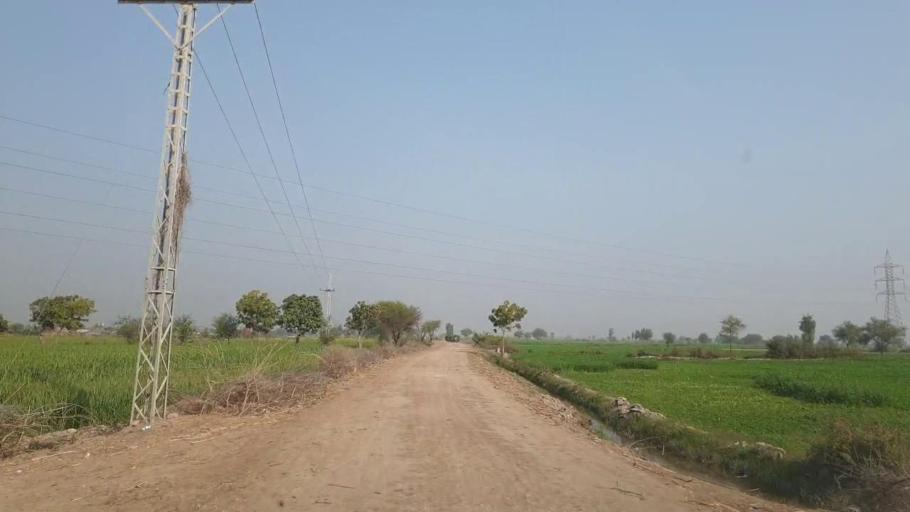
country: PK
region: Sindh
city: Mirpur Khas
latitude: 25.5698
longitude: 69.0157
